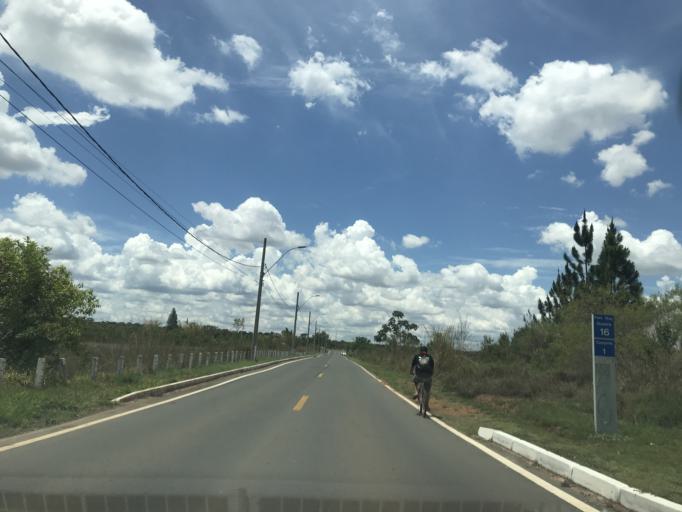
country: BR
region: Federal District
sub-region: Brasilia
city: Brasilia
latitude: -15.8996
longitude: -47.9443
